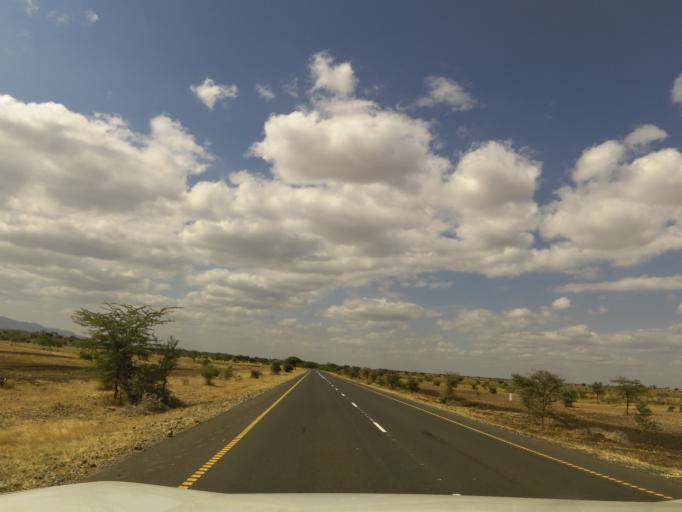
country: TZ
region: Arusha
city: Mto wa Mbu
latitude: -3.5827
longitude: 36.0682
